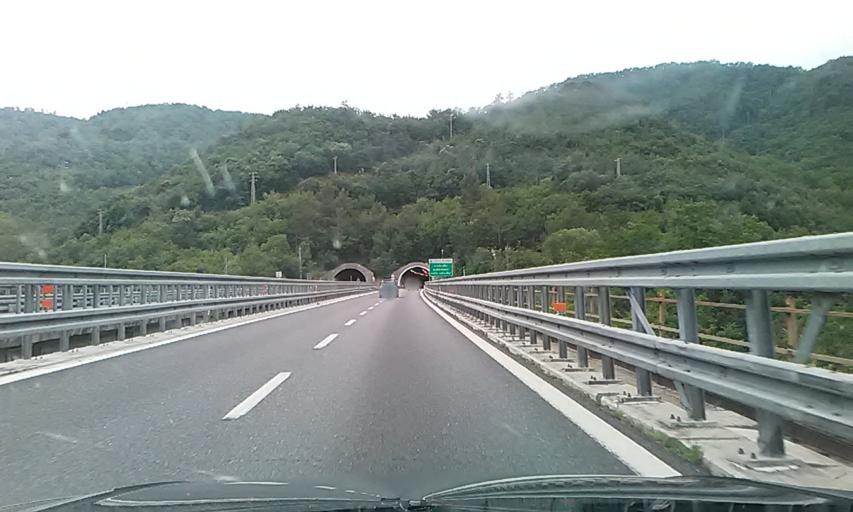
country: IT
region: Liguria
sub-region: Provincia di Savona
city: Villafranca
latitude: 44.0200
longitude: 8.1316
